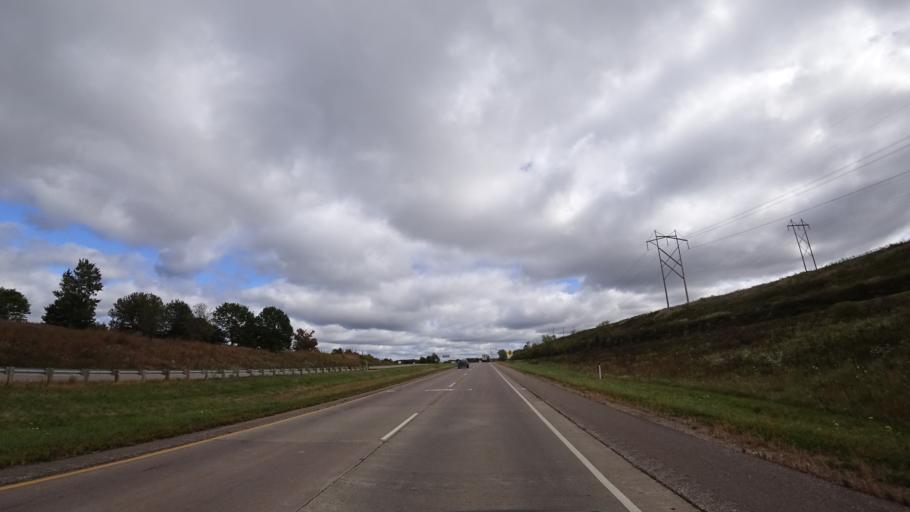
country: US
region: Wisconsin
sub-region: Eau Claire County
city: Eau Claire
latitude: 44.8372
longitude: -91.5446
